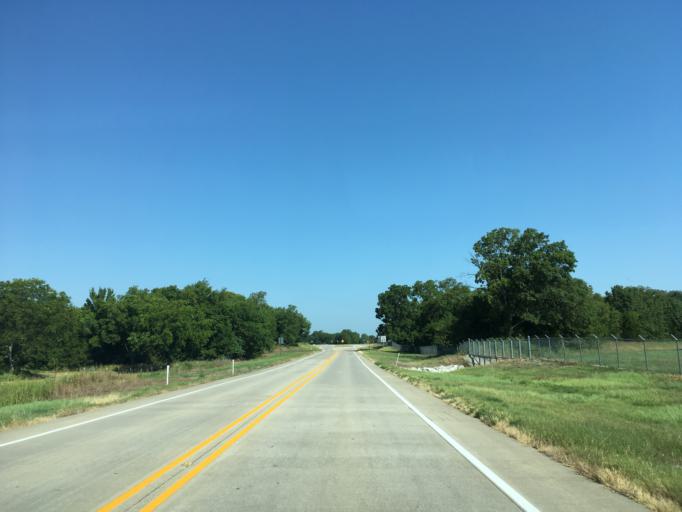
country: US
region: Texas
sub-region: Collin County
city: Fairview
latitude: 33.1623
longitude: -96.5930
